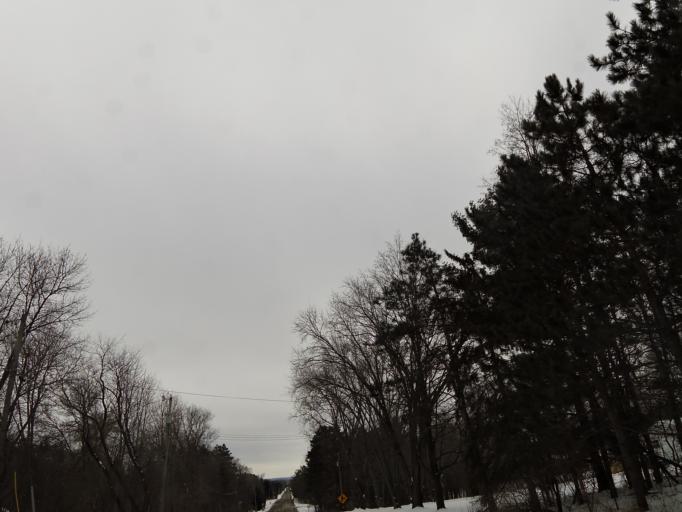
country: US
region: Minnesota
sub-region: Washington County
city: Bayport
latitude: 44.9819
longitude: -92.8224
